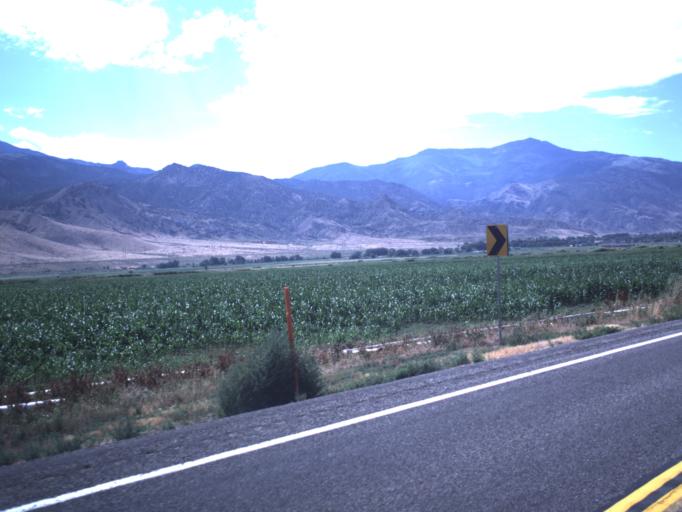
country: US
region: Utah
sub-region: Sevier County
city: Monroe
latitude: 38.6660
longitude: -112.1209
